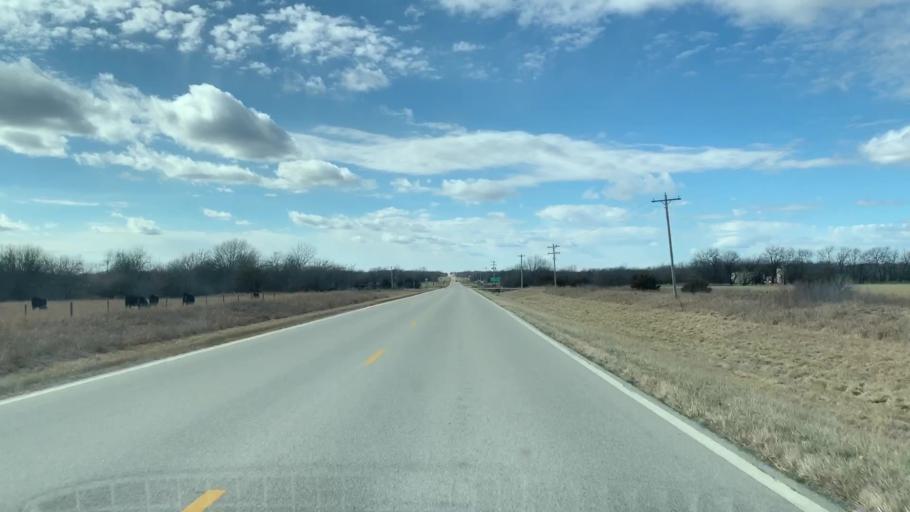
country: US
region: Kansas
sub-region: Neosho County
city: Erie
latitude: 37.5292
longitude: -95.3951
